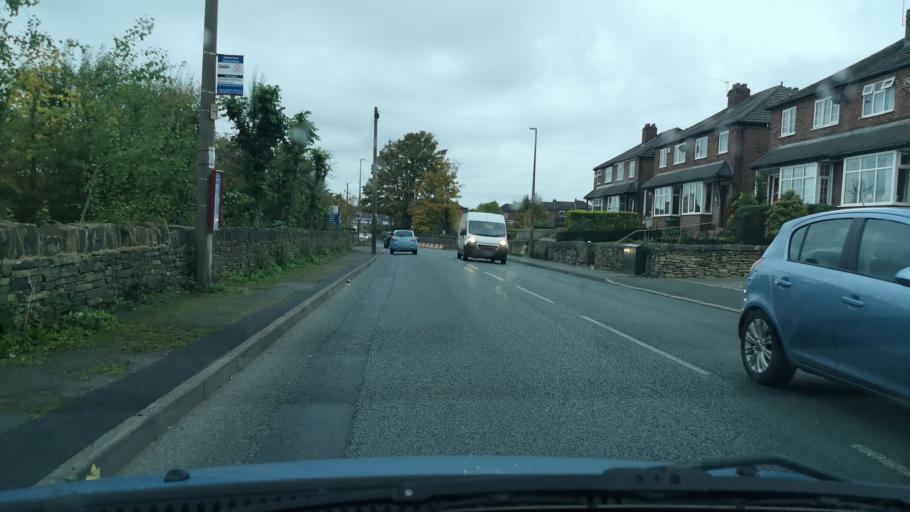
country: GB
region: England
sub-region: Kirklees
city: Heckmondwike
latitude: 53.7021
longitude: -1.6667
